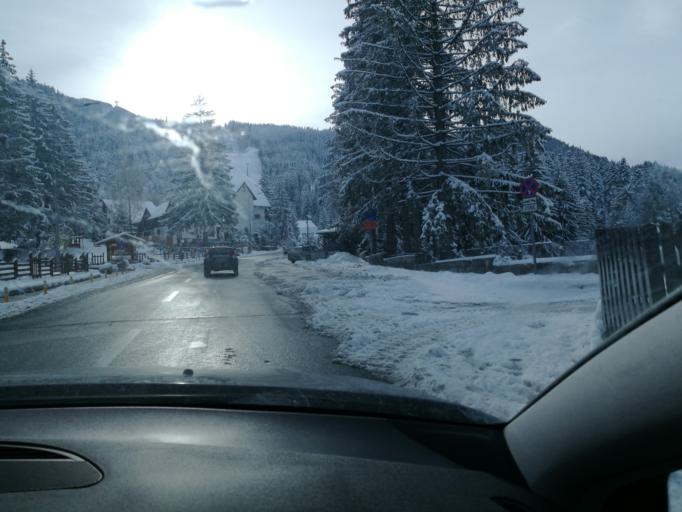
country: RO
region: Brasov
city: Brasov
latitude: 45.5896
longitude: 25.5510
